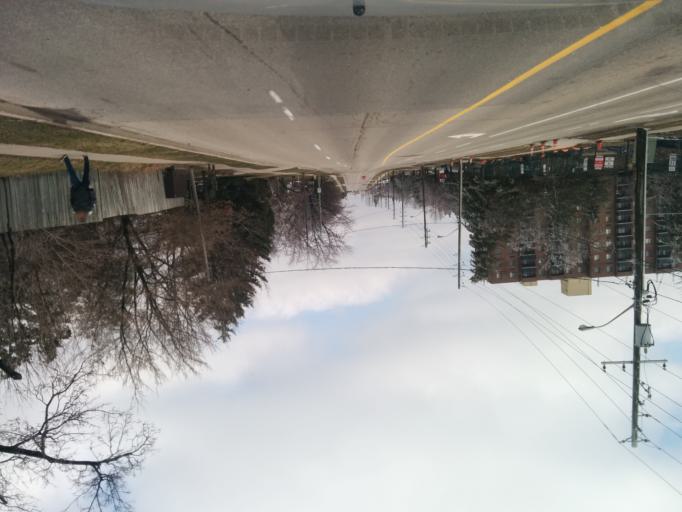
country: CA
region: Ontario
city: Waterloo
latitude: 43.4788
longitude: -80.5353
